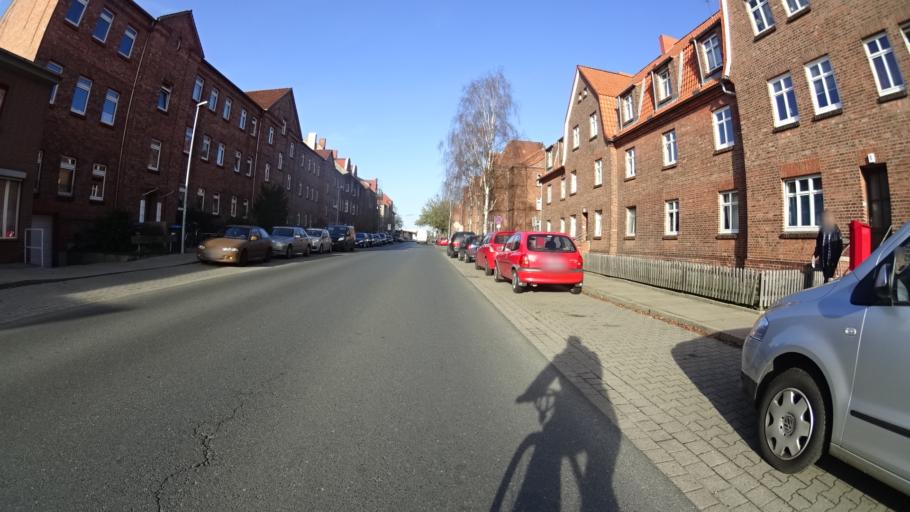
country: DE
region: Lower Saxony
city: Lueneburg
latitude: 53.2518
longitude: 10.4234
